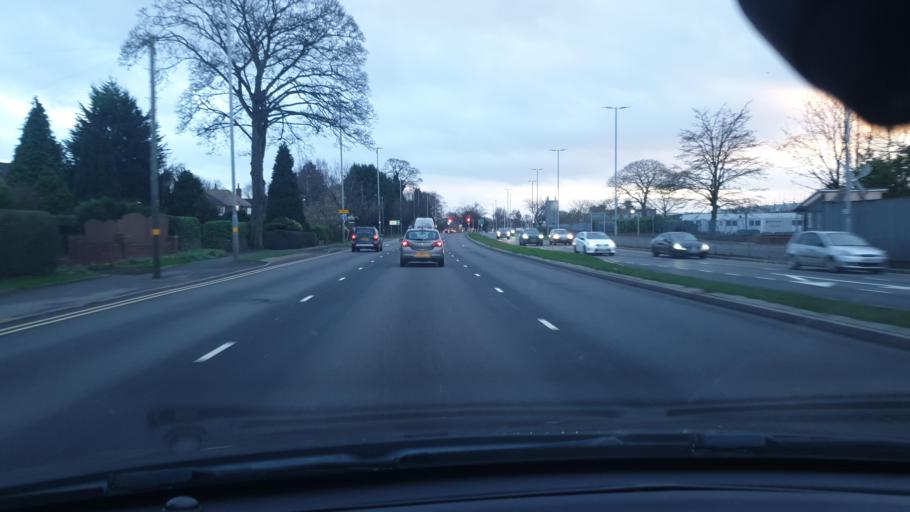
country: GB
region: England
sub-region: Staffordshire
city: Featherstone
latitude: 52.6339
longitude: -2.1249
